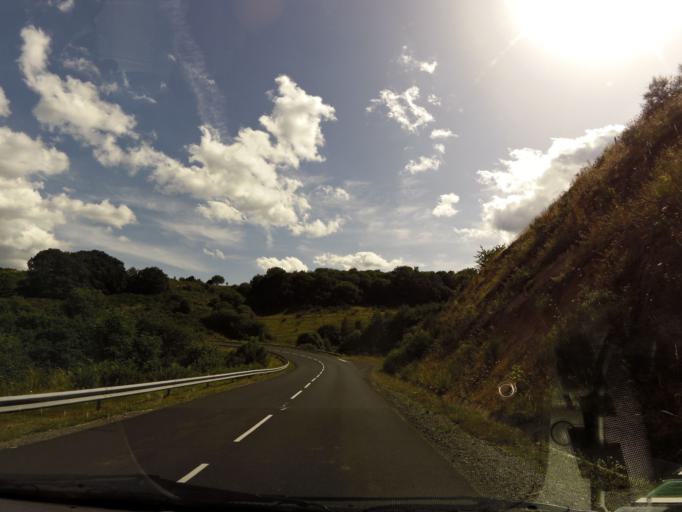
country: FR
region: Auvergne
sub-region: Departement du Puy-de-Dome
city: Aydat
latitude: 45.5431
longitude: 2.9385
